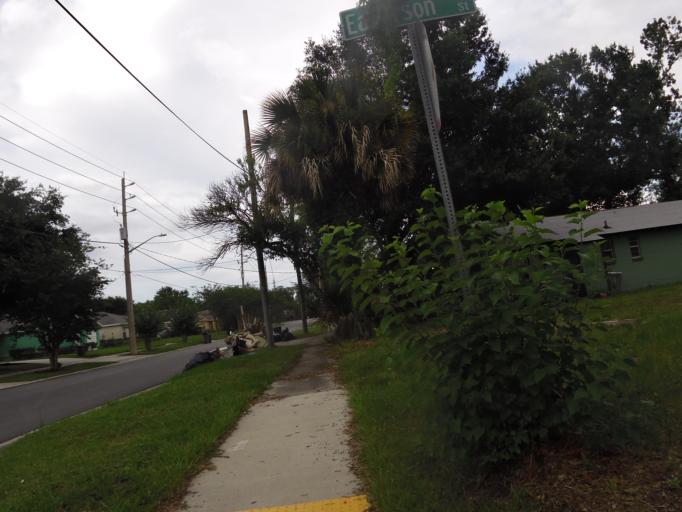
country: US
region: Florida
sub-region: Duval County
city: Jacksonville
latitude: 30.3441
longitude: -81.6727
